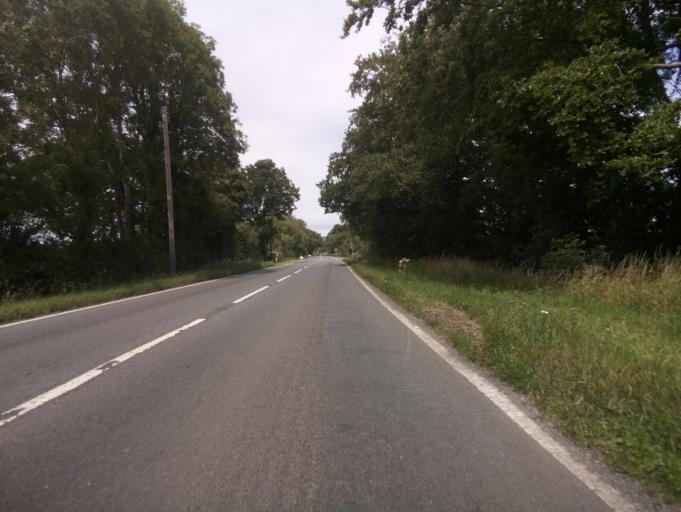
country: GB
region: England
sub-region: Somerset
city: Glastonbury
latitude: 51.1690
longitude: -2.6973
